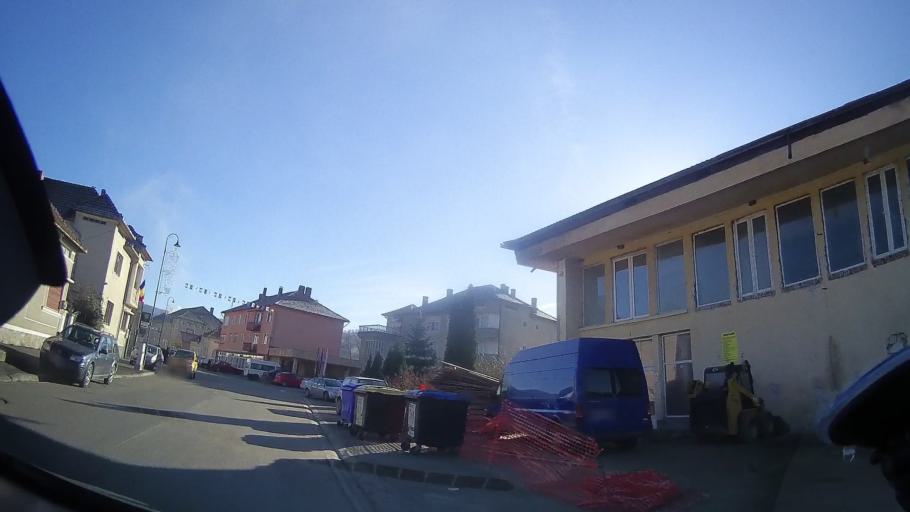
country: RO
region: Bihor
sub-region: Comuna Bratca
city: Bratca
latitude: 46.9277
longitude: 22.5998
